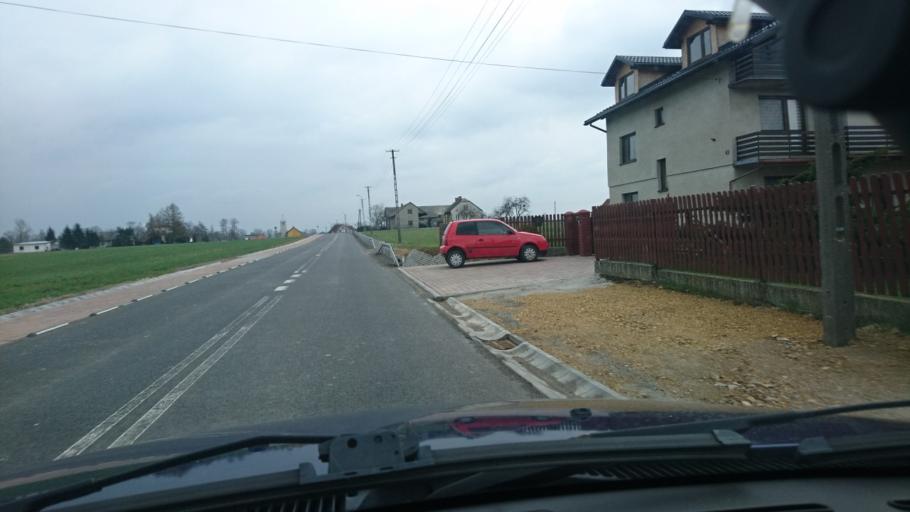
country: PL
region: Silesian Voivodeship
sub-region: Powiat bielski
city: Bronow
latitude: 49.8767
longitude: 18.9088
